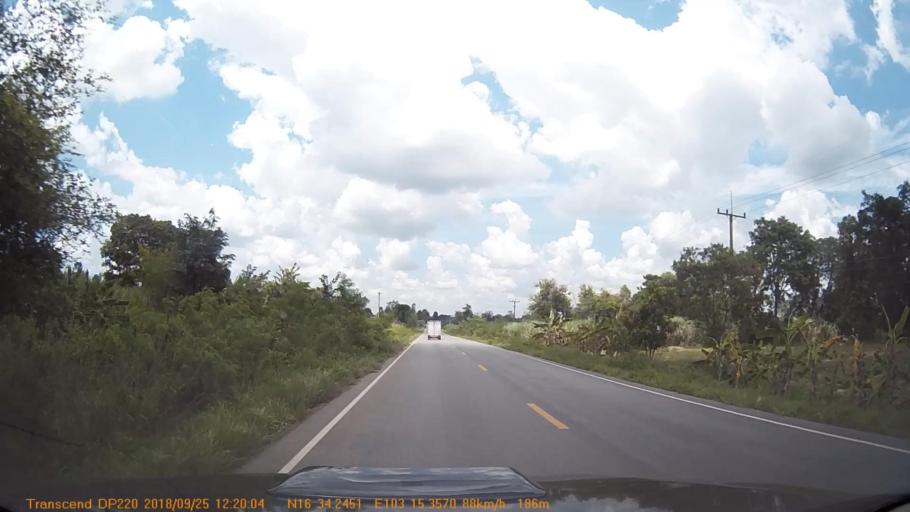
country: TH
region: Kalasin
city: Huai Mek
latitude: 16.5707
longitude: 103.2560
